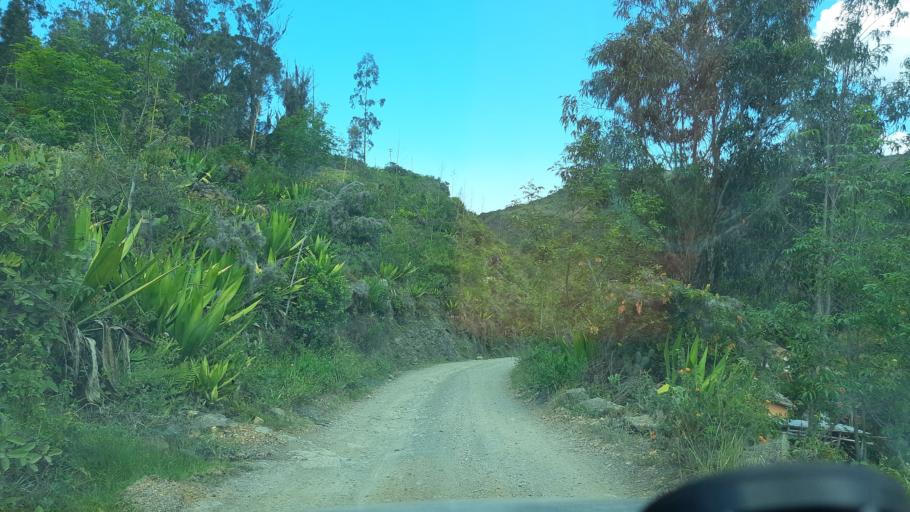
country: CO
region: Boyaca
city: Villa de Leiva
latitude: 5.6782
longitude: -73.5670
